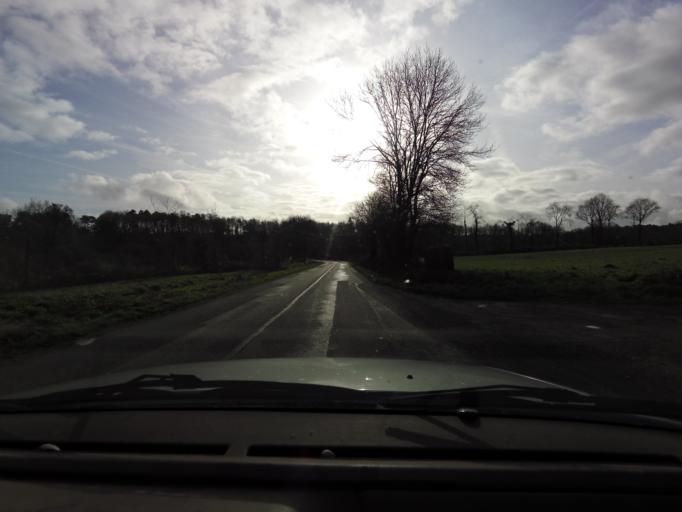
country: FR
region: Brittany
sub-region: Departement du Morbihan
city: Limerzel
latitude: 47.6548
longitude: -2.3598
